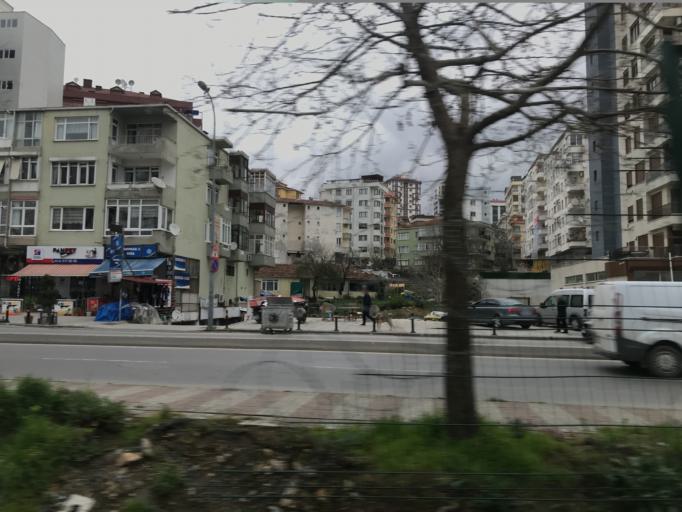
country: TR
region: Istanbul
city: Maltepe
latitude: 40.8960
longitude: 29.1733
